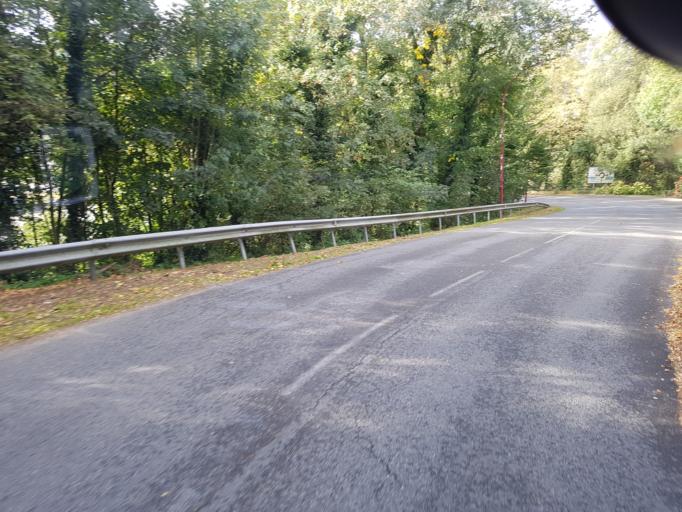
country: FR
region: Midi-Pyrenees
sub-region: Departement du Tarn
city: Pont-de-Larn
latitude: 43.4995
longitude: 2.4019
